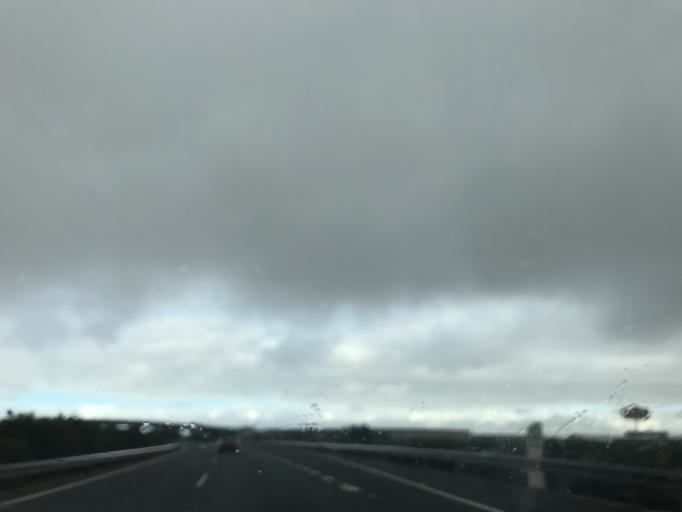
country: ES
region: Andalusia
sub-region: Provincia de Sevilla
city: La Roda de Andalucia
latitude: 37.2212
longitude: -4.7856
